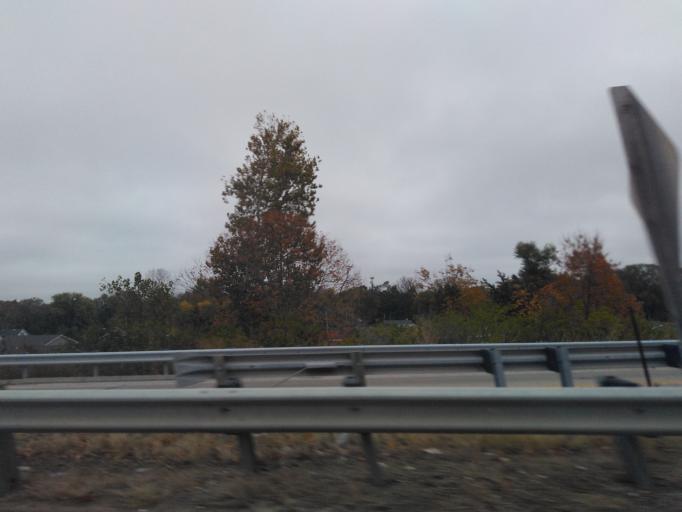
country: US
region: Illinois
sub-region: Saint Clair County
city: Alorton
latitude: 38.5802
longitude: -90.1112
